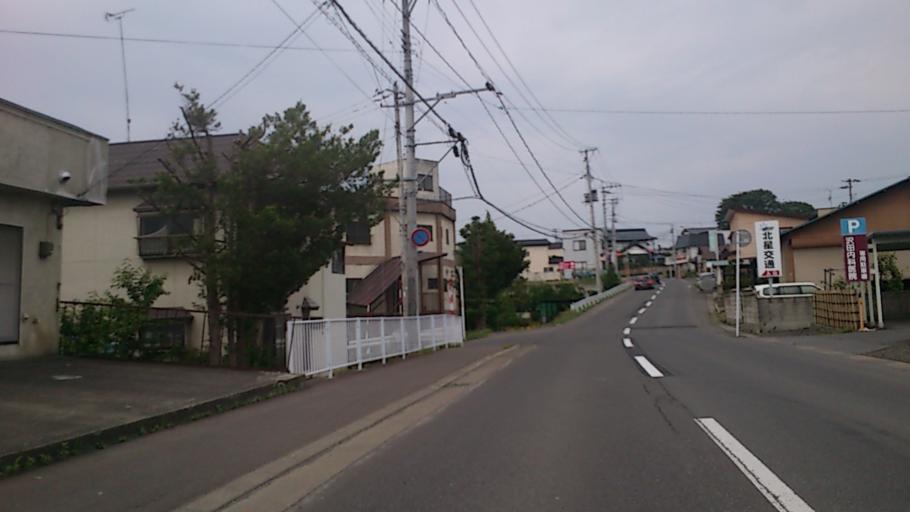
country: JP
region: Aomori
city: Hirosaki
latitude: 40.5945
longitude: 140.4543
